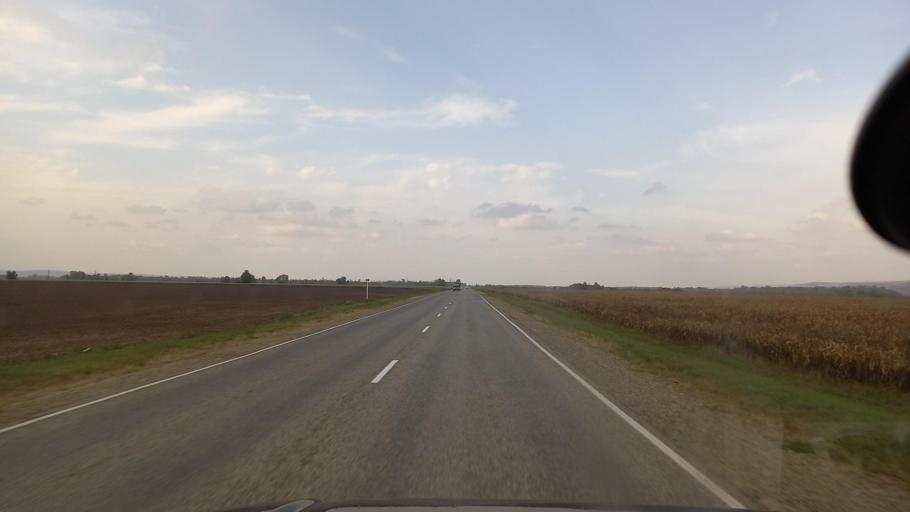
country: RU
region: Krasnodarskiy
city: Perepravnaya
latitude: 44.3524
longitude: 40.8384
